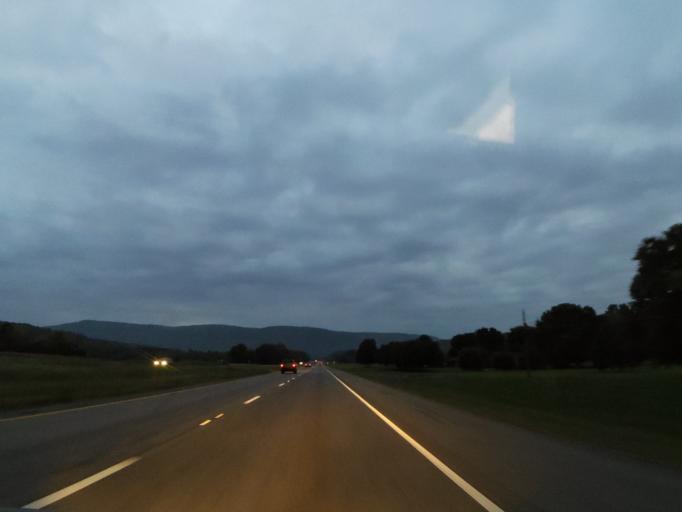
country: US
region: Alabama
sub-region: Madison County
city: Owens Cross Roads
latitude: 34.6890
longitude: -86.3489
